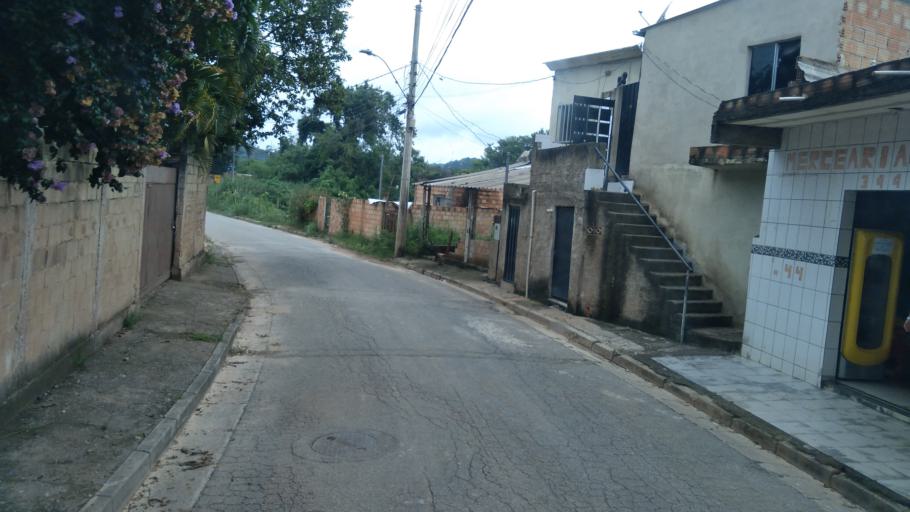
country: BR
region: Minas Gerais
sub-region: Santa Luzia
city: Santa Luzia
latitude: -19.8384
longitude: -43.8649
